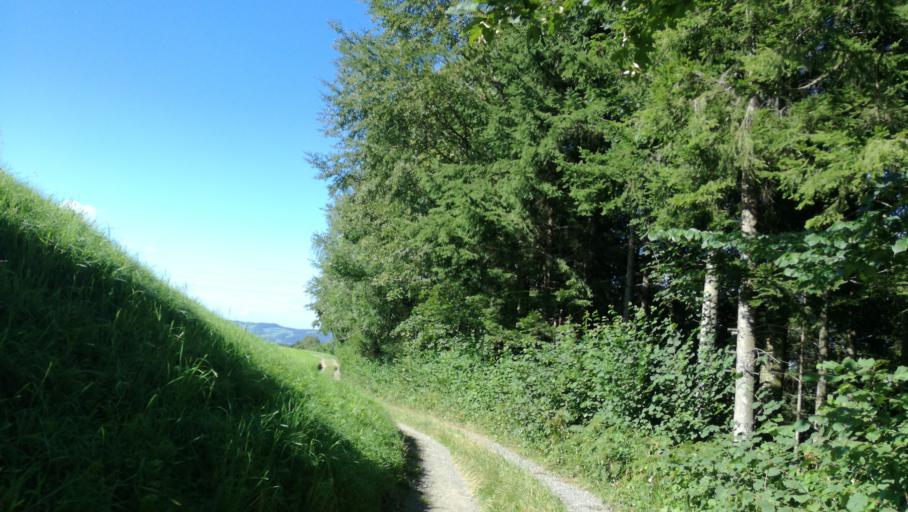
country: CH
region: Zug
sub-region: Zug
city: Unterageri
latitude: 47.1573
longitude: 8.5553
